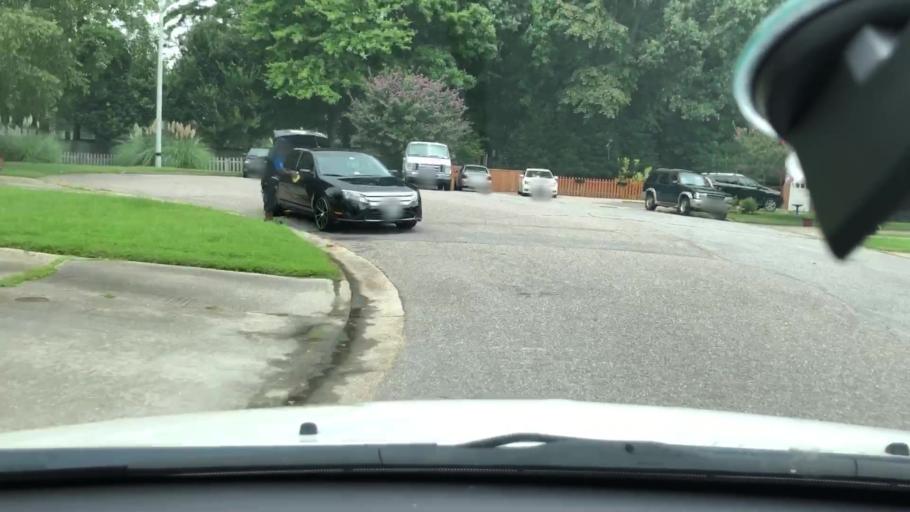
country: US
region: Virginia
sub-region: City of Virginia Beach
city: Virginia Beach
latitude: 36.8457
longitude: -76.1179
